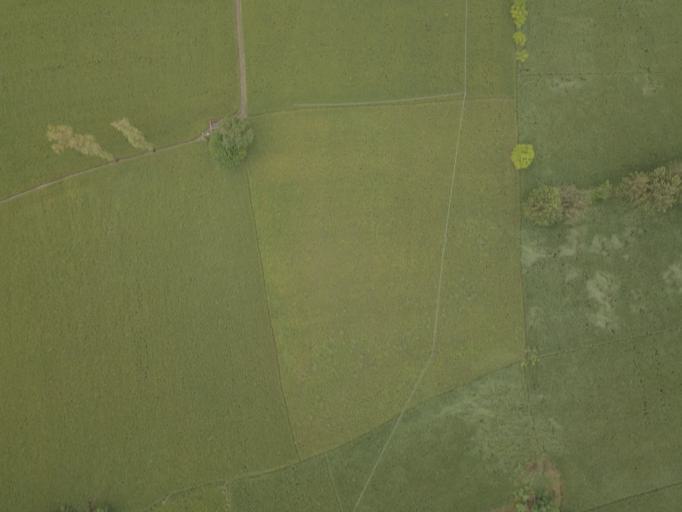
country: IN
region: Punjab
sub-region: Shahid Bhagat Singh Nagar
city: Rahon
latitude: 31.0176
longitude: 76.0921
